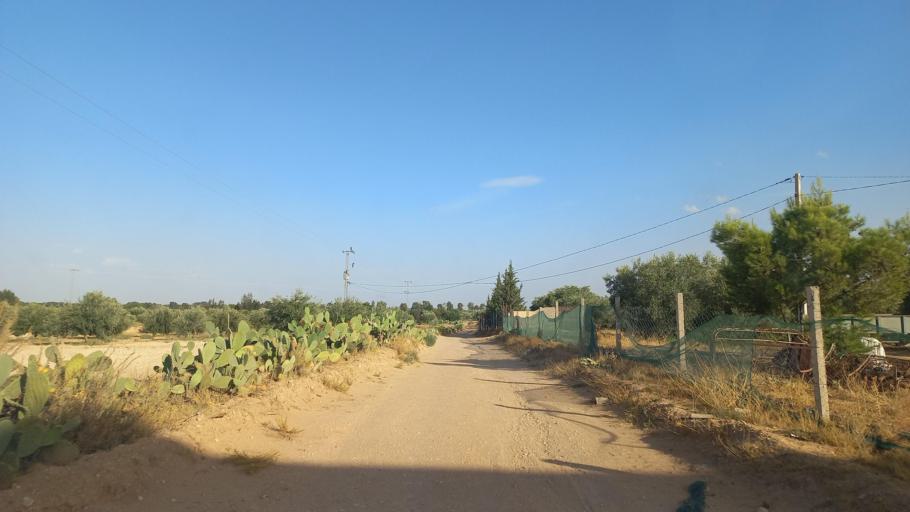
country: TN
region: Al Qasrayn
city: Kasserine
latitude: 35.2648
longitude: 9.0237
